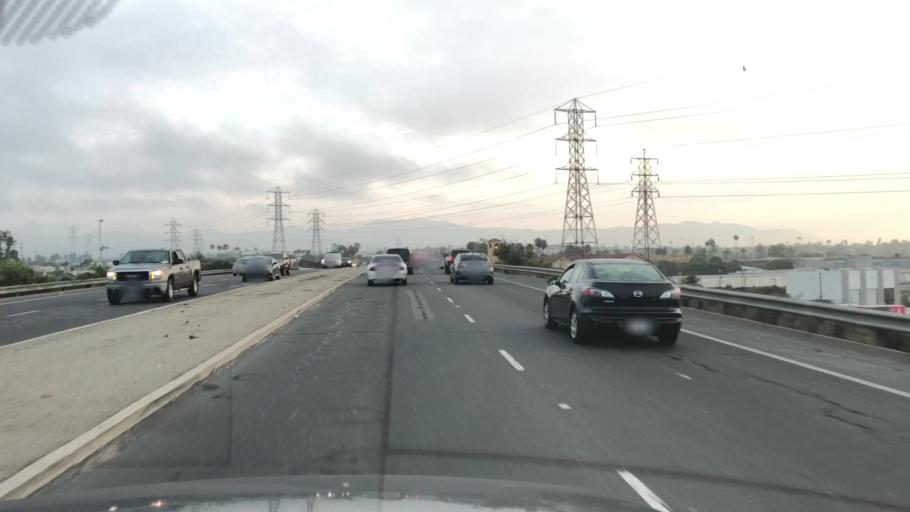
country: US
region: California
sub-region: Ventura County
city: El Rio
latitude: 34.2476
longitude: -119.2134
